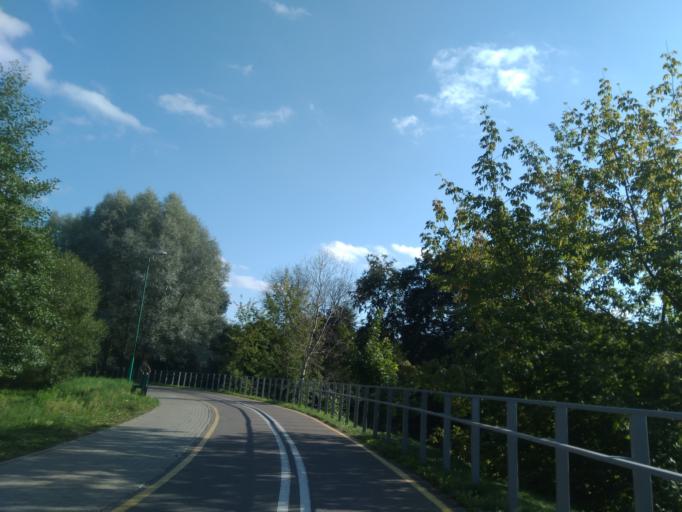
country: BY
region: Minsk
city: Minsk
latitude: 53.8722
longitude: 27.5836
